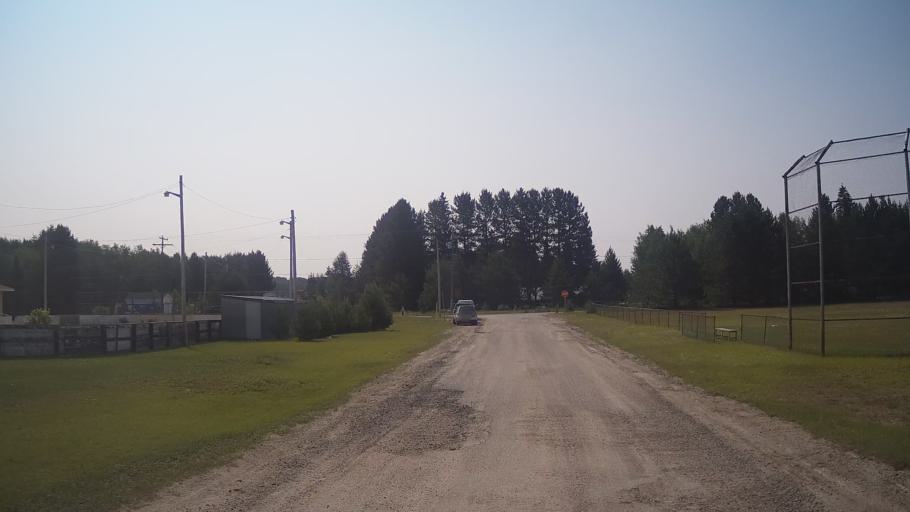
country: CA
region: Ontario
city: Timmins
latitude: 47.6776
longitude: -81.7190
